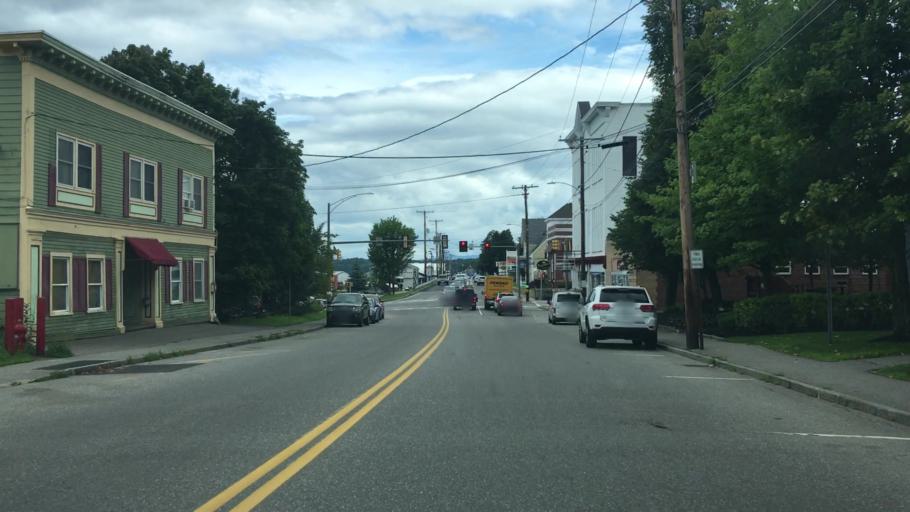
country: US
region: New Hampshire
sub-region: Belknap County
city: Laconia
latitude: 43.5466
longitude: -71.4631
